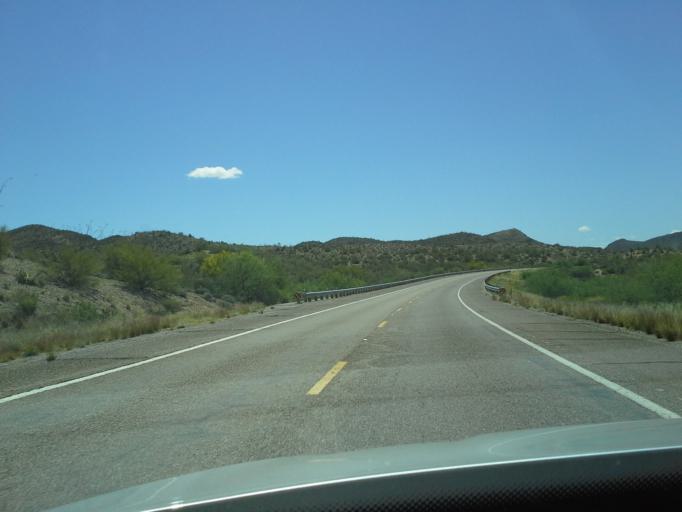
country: US
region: Arizona
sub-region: Pinal County
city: Superior
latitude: 33.2700
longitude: -111.0964
